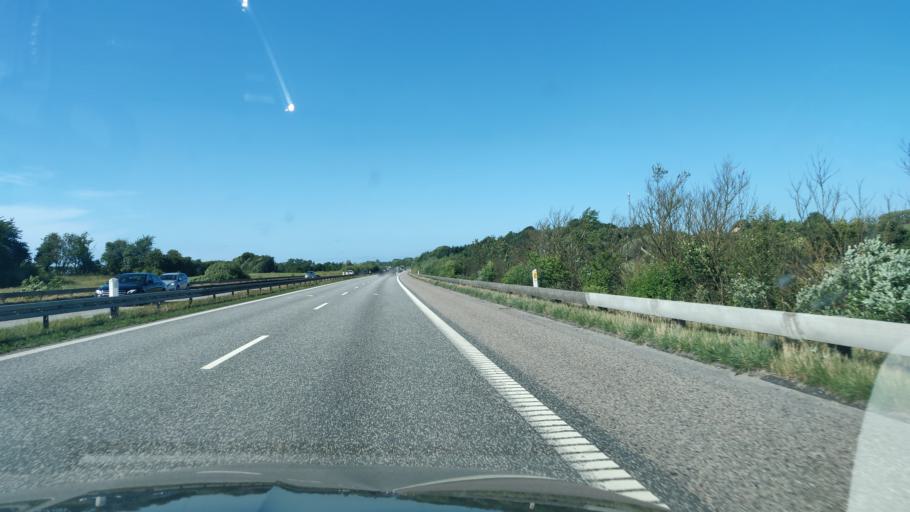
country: DK
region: North Denmark
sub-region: Mariagerfjord Kommune
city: Hobro
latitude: 56.6955
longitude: 9.7291
